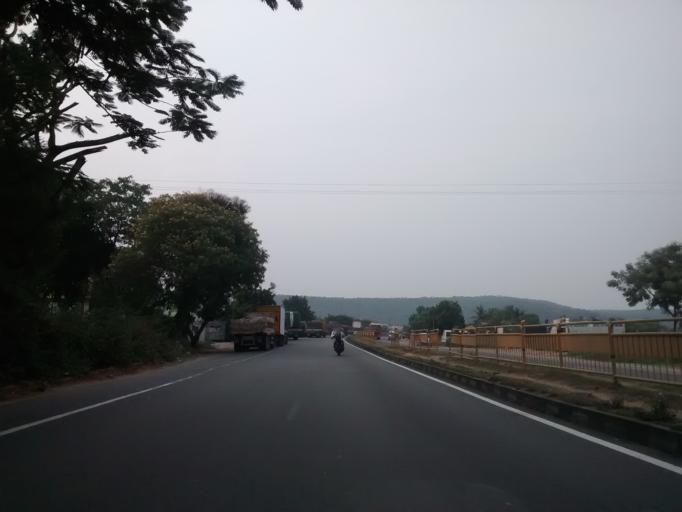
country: IN
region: Tamil Nadu
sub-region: Salem
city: Omalur
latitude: 11.9429
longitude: 78.0490
